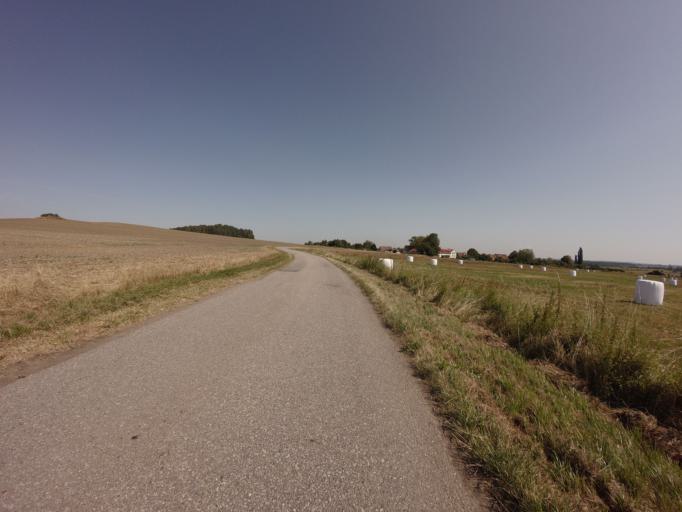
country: CZ
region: Jihocesky
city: Kamenny Ujezd
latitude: 48.8807
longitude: 14.3841
